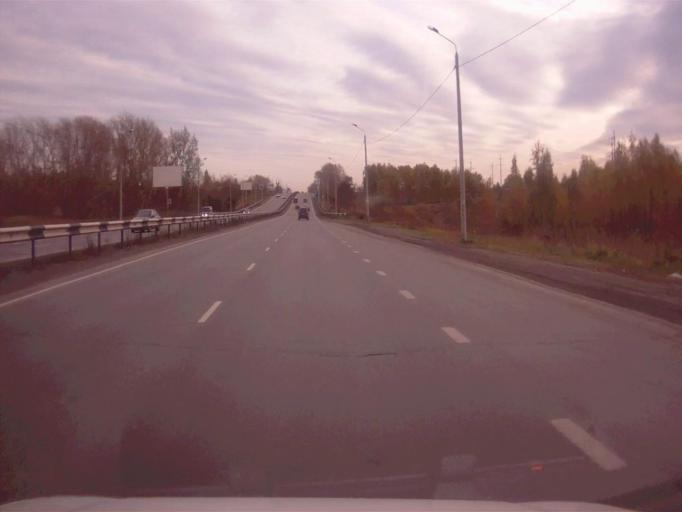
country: RU
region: Chelyabinsk
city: Novosineglazovskiy
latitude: 55.0592
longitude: 61.4033
